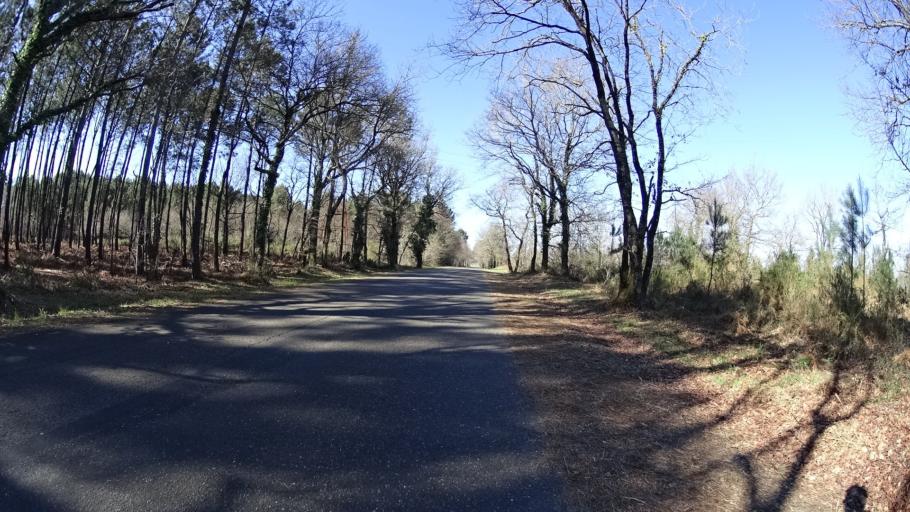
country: FR
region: Aquitaine
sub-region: Departement des Landes
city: Mees
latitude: 43.7321
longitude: -1.0941
